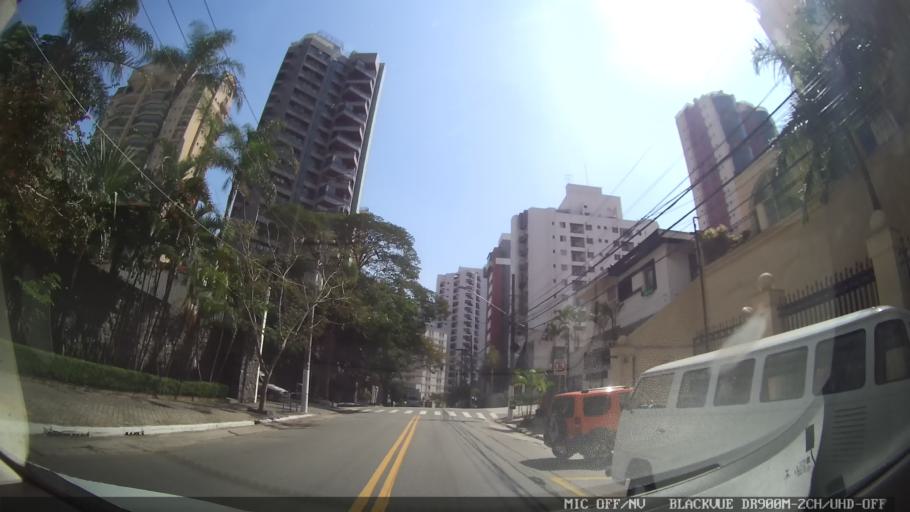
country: BR
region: Sao Paulo
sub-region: Sao Paulo
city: Sao Paulo
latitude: -23.4914
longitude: -46.6293
